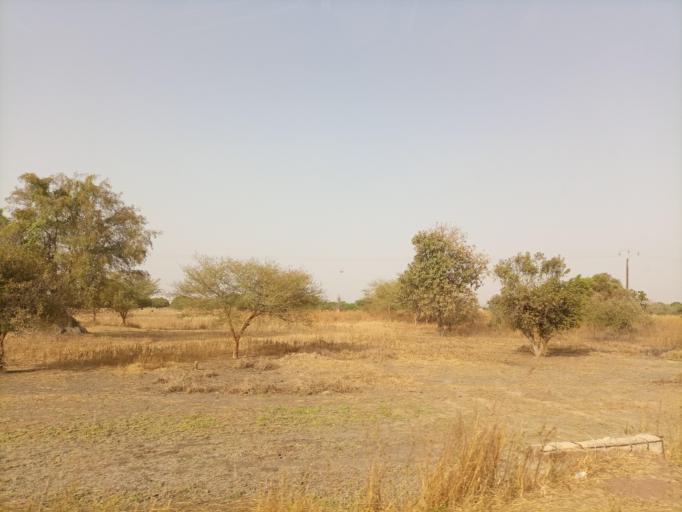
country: SN
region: Fatick
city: Passi
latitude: 14.0242
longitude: -16.3013
